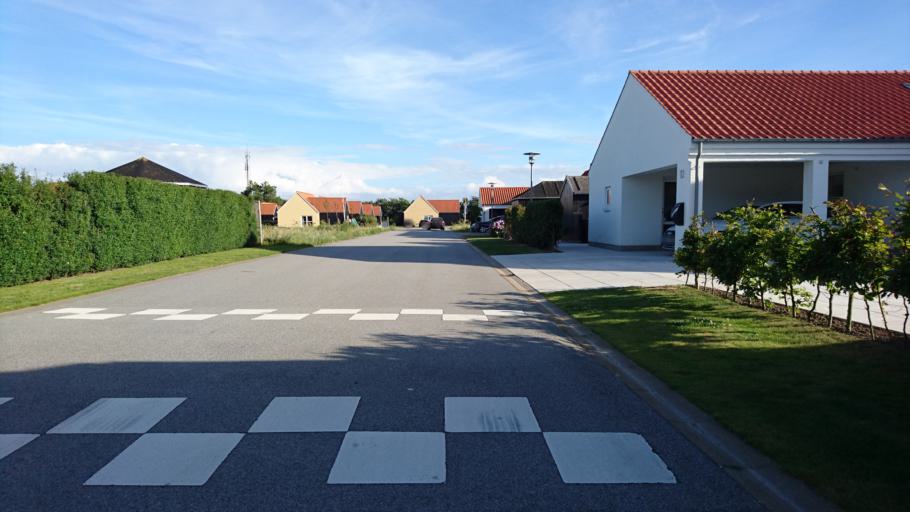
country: DK
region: North Denmark
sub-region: Frederikshavn Kommune
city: Skagen
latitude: 57.7330
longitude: 10.5915
